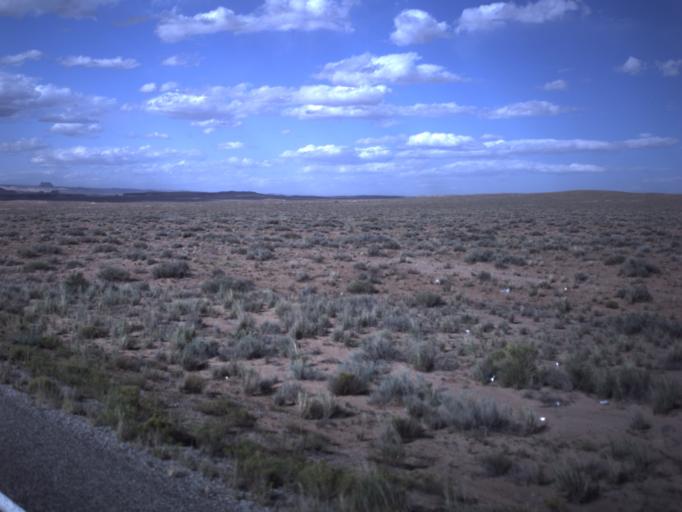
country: US
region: Utah
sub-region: Emery County
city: Ferron
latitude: 38.3473
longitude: -110.6935
